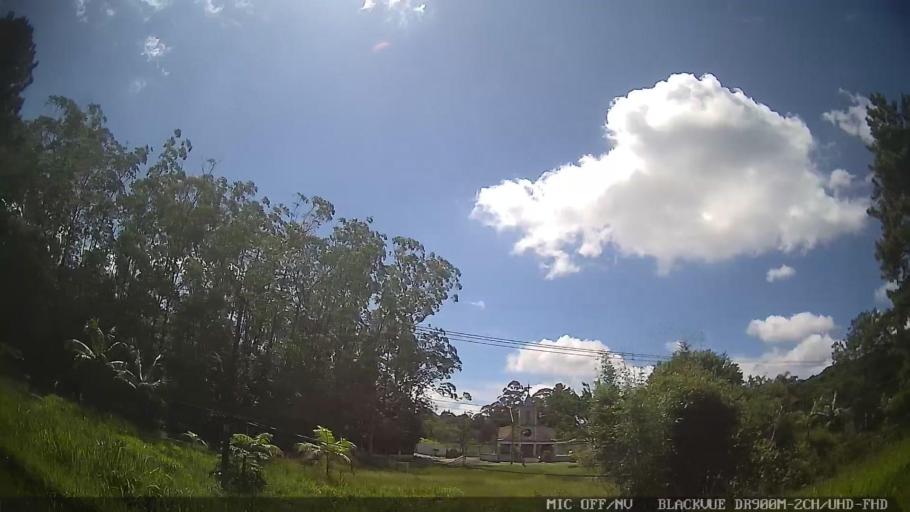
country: BR
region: Sao Paulo
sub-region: Mogi das Cruzes
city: Mogi das Cruzes
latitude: -23.6574
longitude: -46.2022
